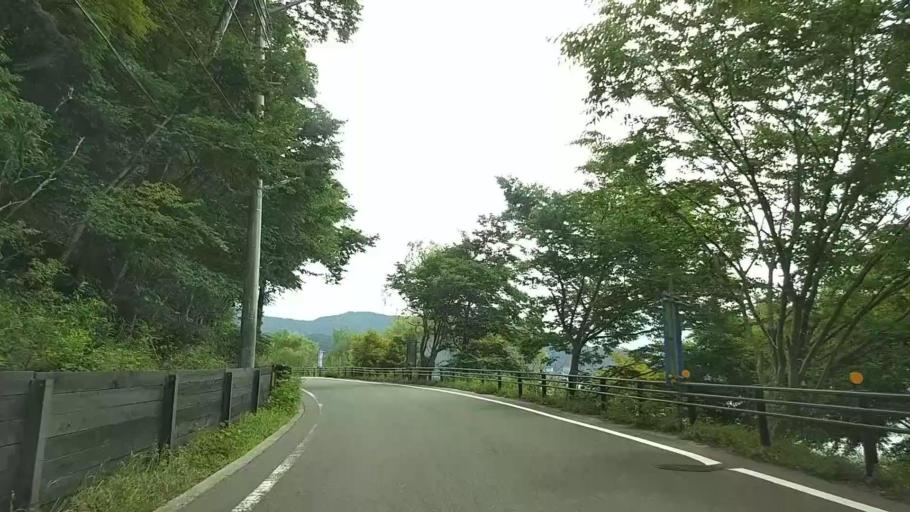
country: JP
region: Yamanashi
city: Fujikawaguchiko
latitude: 35.5229
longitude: 138.7517
